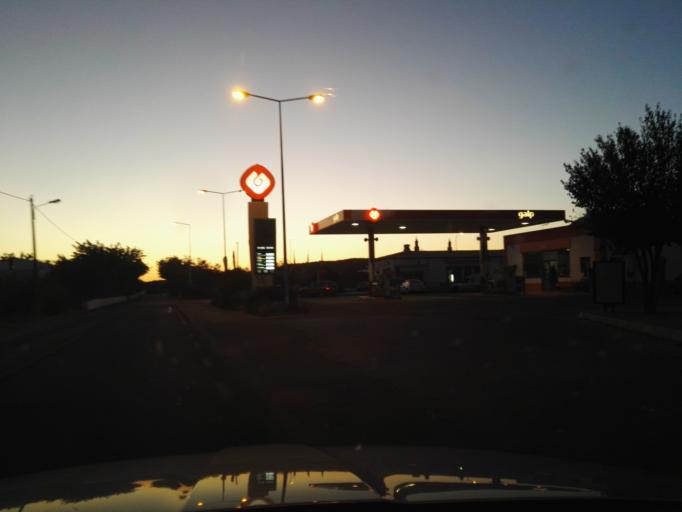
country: PT
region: Faro
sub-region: Faro
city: Santa Barbara de Nexe
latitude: 37.1507
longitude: -7.9396
